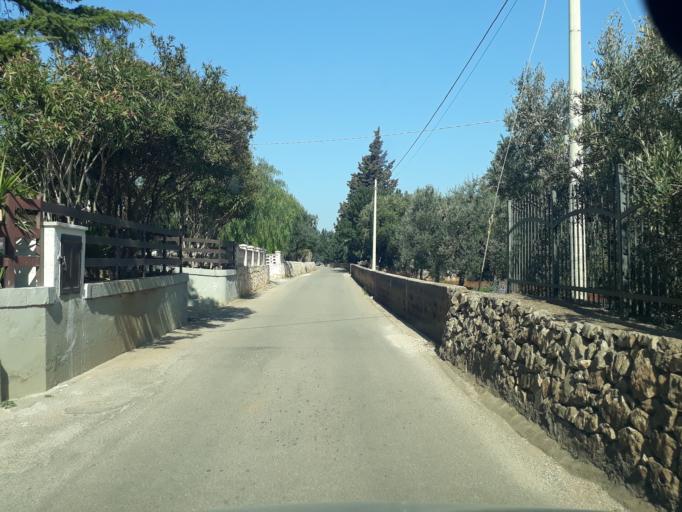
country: IT
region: Apulia
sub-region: Provincia di Brindisi
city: Fasano
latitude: 40.8394
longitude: 17.3474
